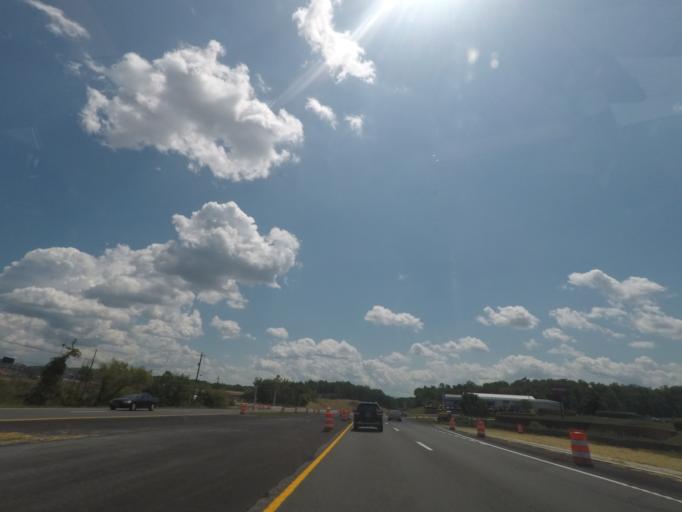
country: US
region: Virginia
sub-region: City of Winchester
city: Winchester
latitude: 39.1415
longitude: -78.1252
